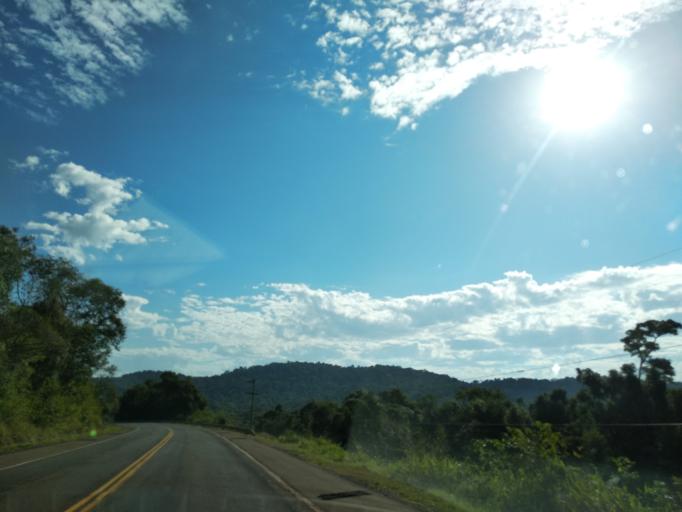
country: AR
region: Misiones
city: Aristobulo del Valle
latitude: -27.0919
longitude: -54.9477
